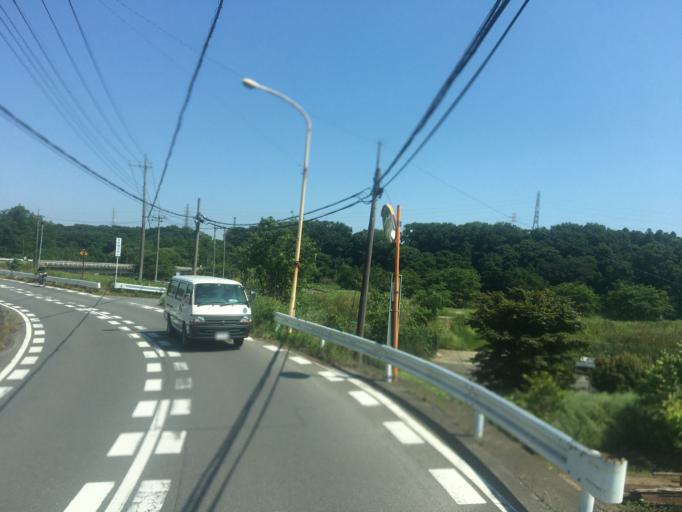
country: JP
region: Saitama
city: Ogawa
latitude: 36.0309
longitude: 139.3318
